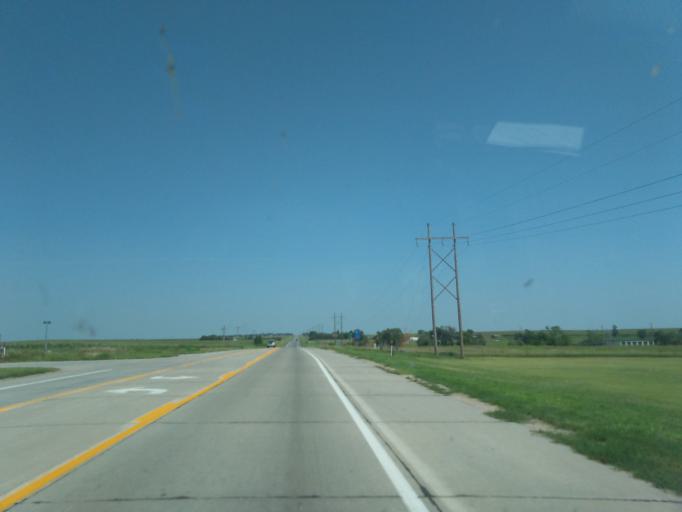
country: US
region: Nebraska
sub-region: Red Willow County
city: McCook
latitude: 40.2293
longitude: -100.6499
